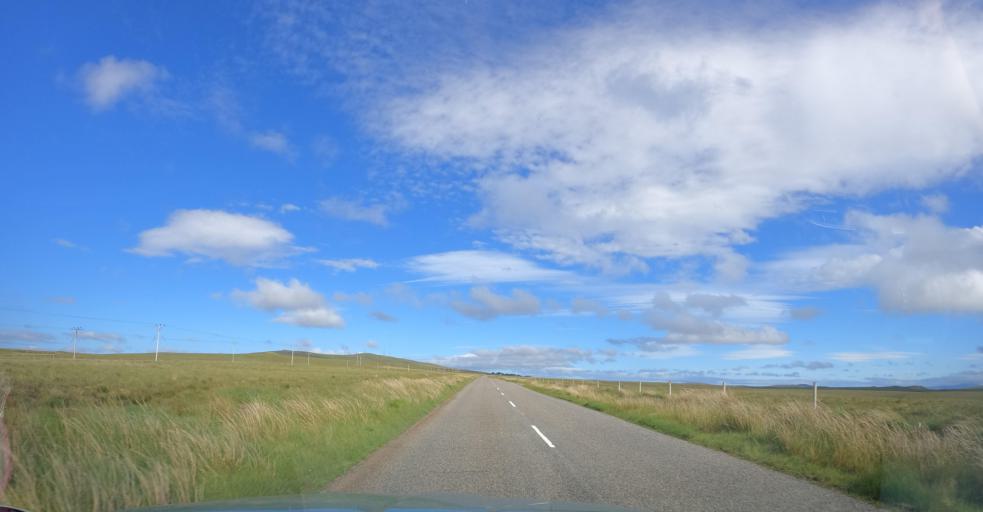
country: GB
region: Scotland
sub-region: Eilean Siar
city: Isle of Lewis
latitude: 58.1783
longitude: -6.6357
